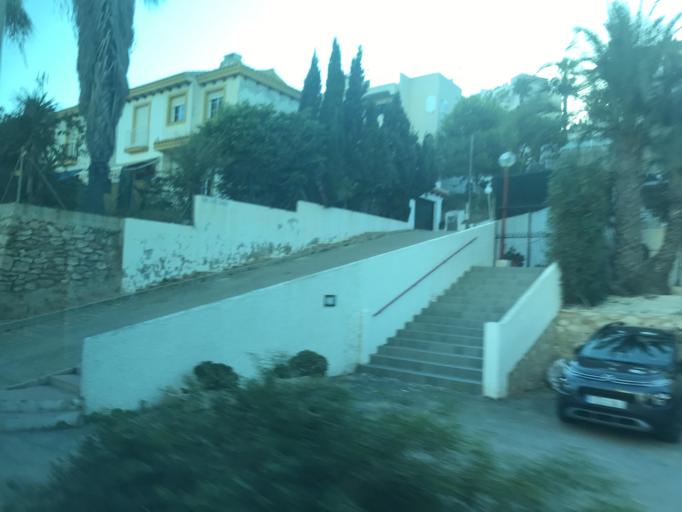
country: ES
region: Valencia
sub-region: Provincia de Alicante
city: Torrevieja
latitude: 38.0026
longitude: -0.6505
